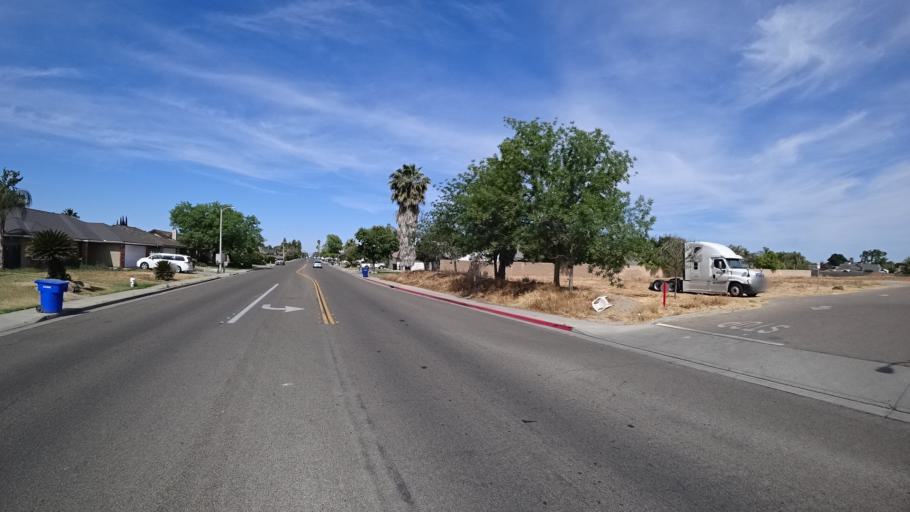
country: US
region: California
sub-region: Kings County
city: Hanford
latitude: 36.3573
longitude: -119.6382
